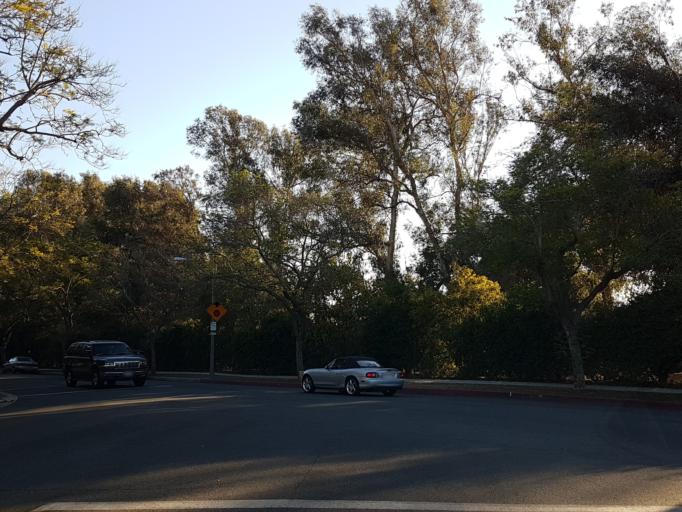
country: US
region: California
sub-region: Los Angeles County
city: Century City
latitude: 34.0714
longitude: -118.4176
